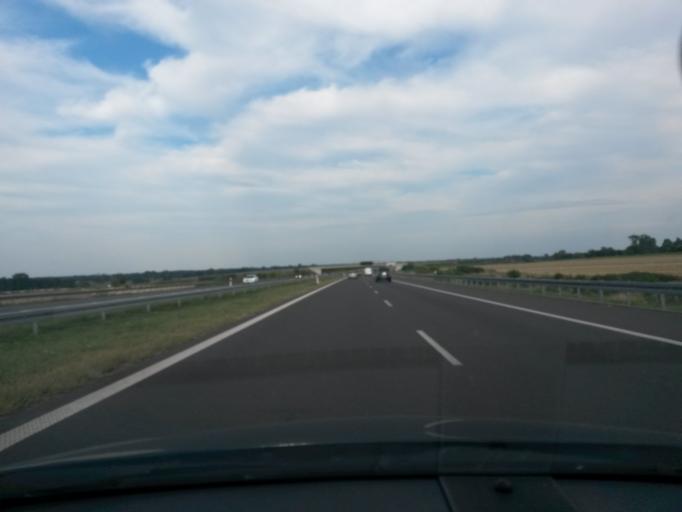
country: PL
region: Greater Poland Voivodeship
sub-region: Powiat kolski
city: Koscielec
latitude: 52.1421
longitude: 18.5832
